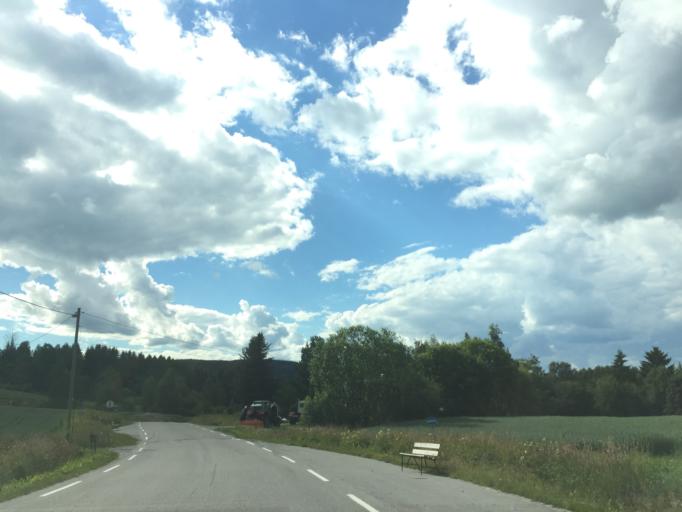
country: NO
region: Hedmark
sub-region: Kongsvinger
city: Spetalen
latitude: 60.1929
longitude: 11.8395
